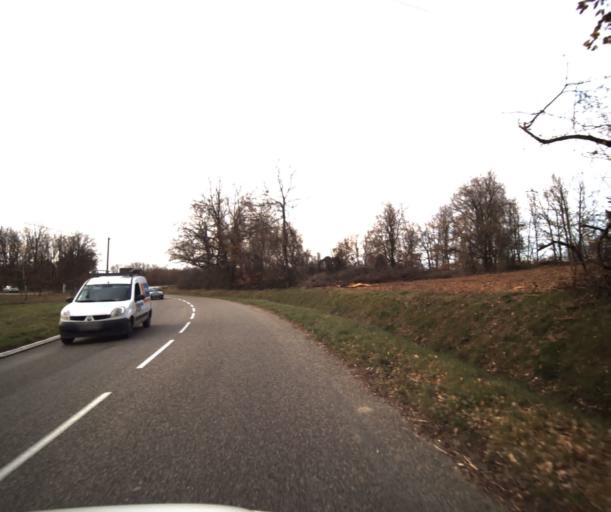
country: FR
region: Midi-Pyrenees
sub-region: Departement du Tarn-et-Garonne
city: Campsas
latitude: 43.9020
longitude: 1.3022
